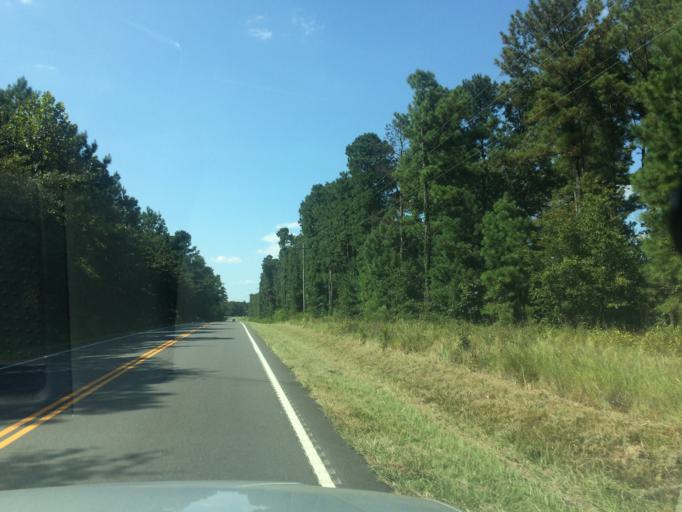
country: US
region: South Carolina
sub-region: Lexington County
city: Batesburg-Leesville
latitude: 33.7070
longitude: -81.4886
